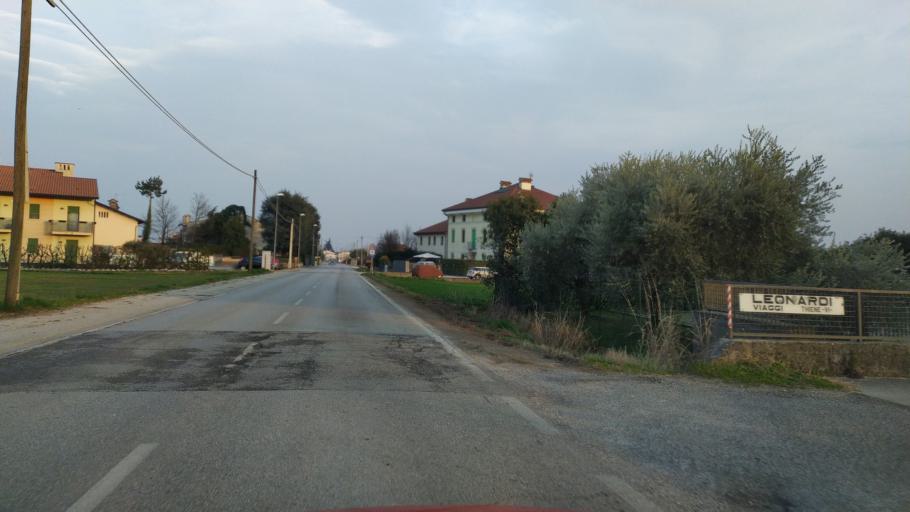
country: IT
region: Veneto
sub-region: Provincia di Vicenza
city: Sarcedo
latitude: 45.6899
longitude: 11.5070
